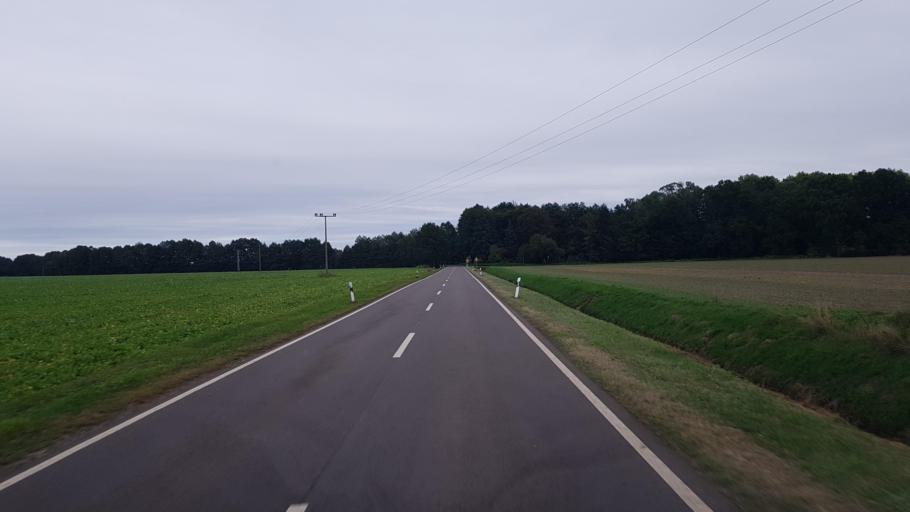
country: DE
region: Brandenburg
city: Drahnsdorf
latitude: 51.8953
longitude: 13.6384
